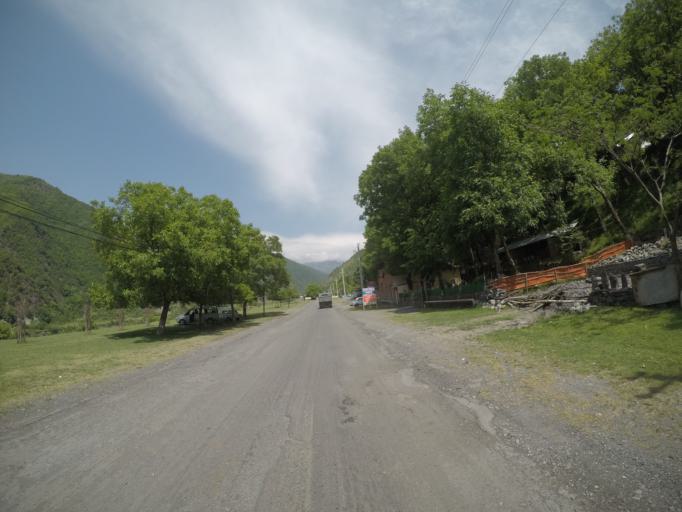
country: AZ
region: Qakh Rayon
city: Qaxbas
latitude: 41.4650
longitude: 47.0415
